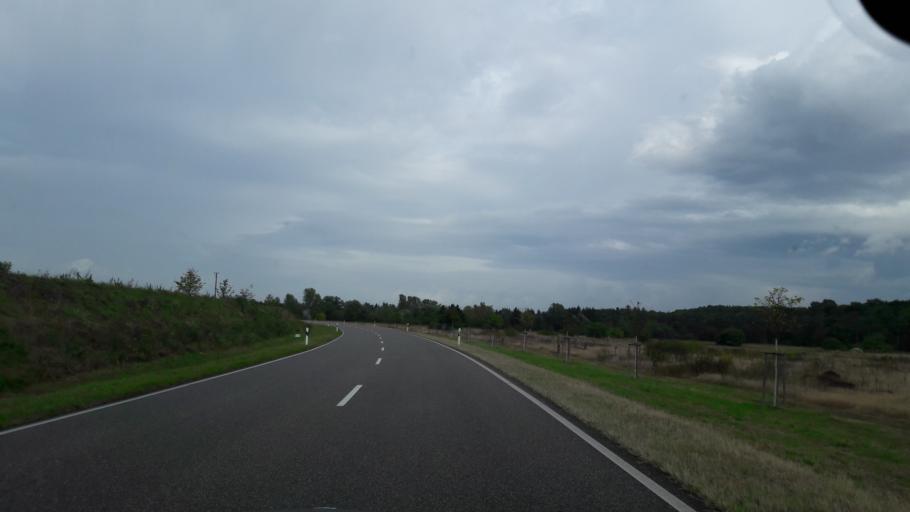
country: DE
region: Baden-Wuerttemberg
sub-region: Karlsruhe Region
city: Sankt Leon-Rot
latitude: 49.2566
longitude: 8.6456
